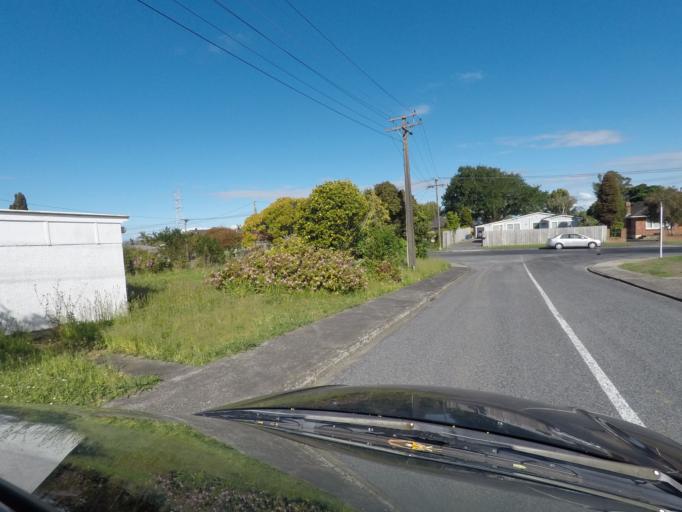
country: NZ
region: Auckland
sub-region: Auckland
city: Rosebank
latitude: -36.8701
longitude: 174.6482
